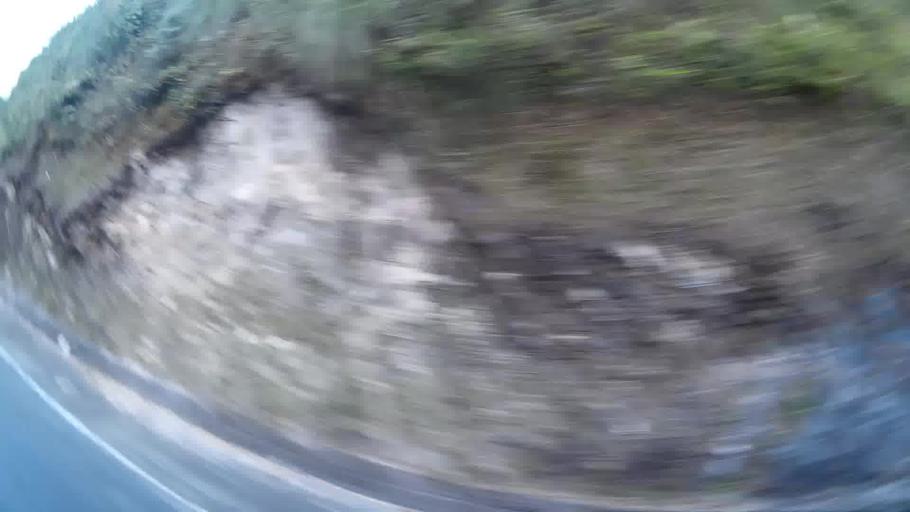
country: CO
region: Quindio
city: Filandia
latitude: 4.7370
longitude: -75.6461
